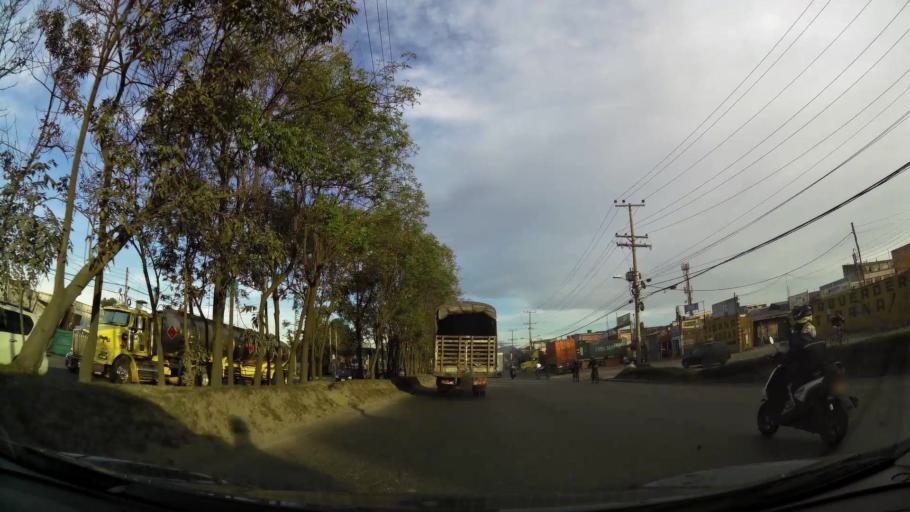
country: CO
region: Cundinamarca
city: Funza
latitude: 4.6952
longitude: -74.1700
